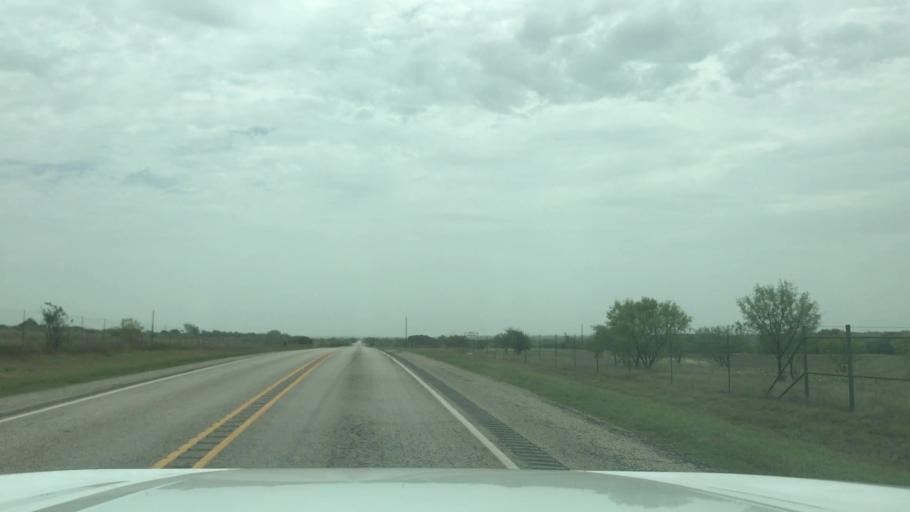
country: US
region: Texas
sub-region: Hamilton County
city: Hico
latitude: 32.0537
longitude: -98.1738
